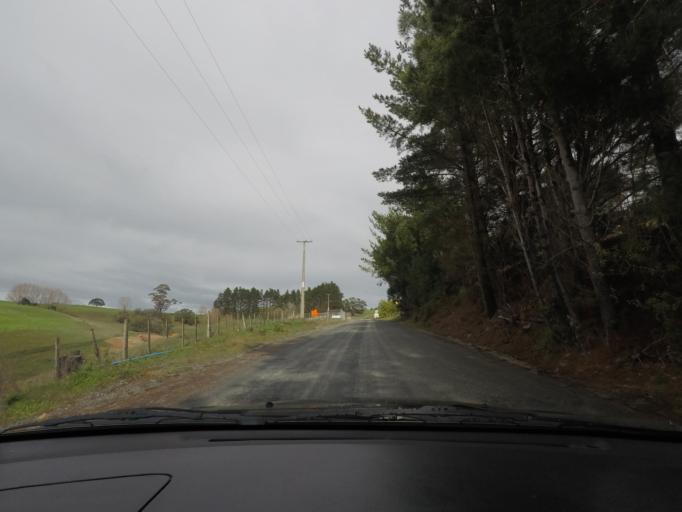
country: NZ
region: Auckland
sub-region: Auckland
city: Warkworth
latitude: -36.4503
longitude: 174.7502
